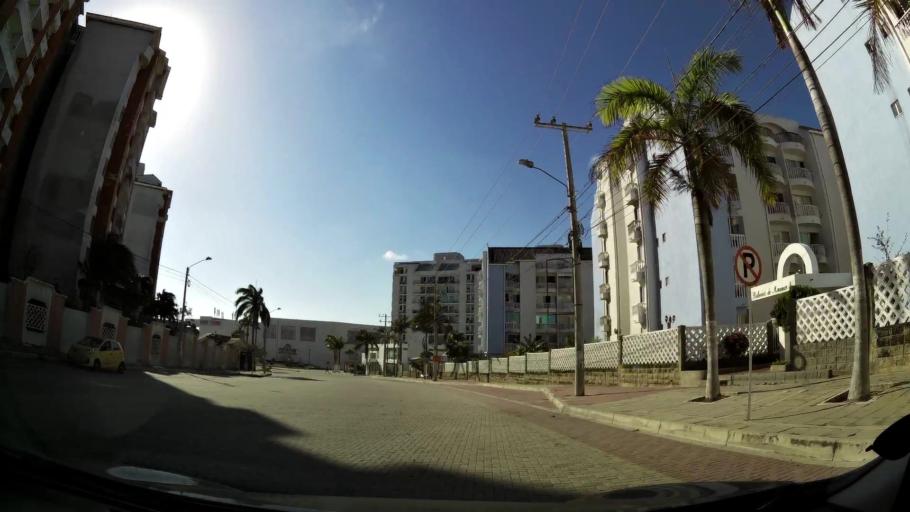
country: CO
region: Atlantico
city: Barranquilla
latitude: 11.0033
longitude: -74.8335
